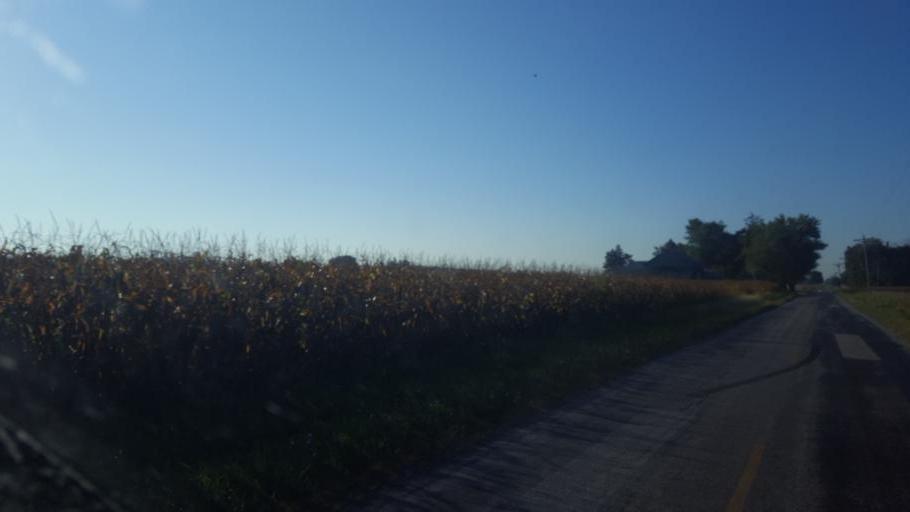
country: US
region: Ohio
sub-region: Morrow County
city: Cardington
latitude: 40.5386
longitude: -82.9956
